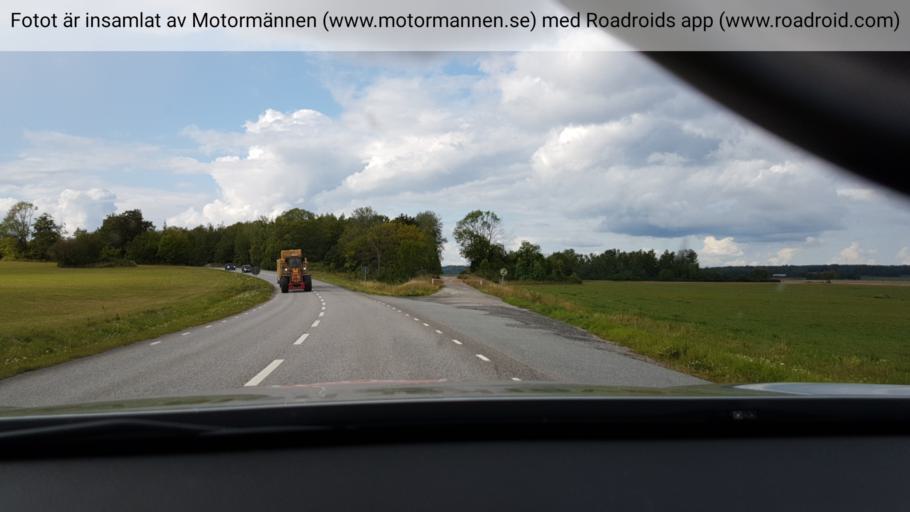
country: SE
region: Stockholm
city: Stenhamra
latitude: 59.3341
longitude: 17.7444
